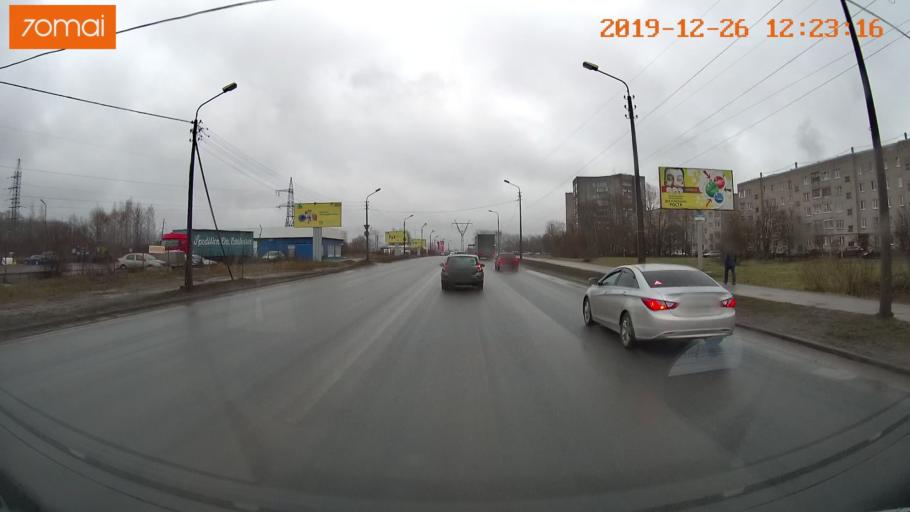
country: RU
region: Vologda
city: Tonshalovo
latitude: 59.1497
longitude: 37.9556
